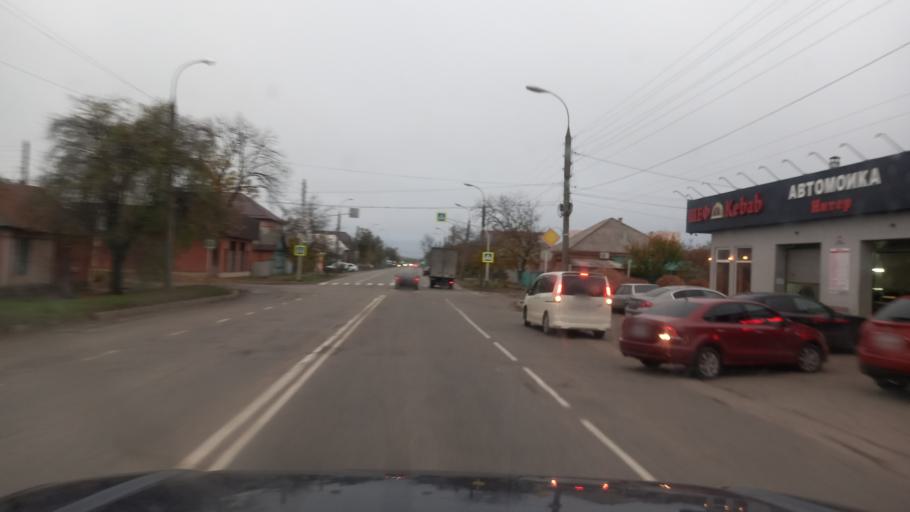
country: RU
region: Adygeya
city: Maykop
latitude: 44.6210
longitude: 40.0752
